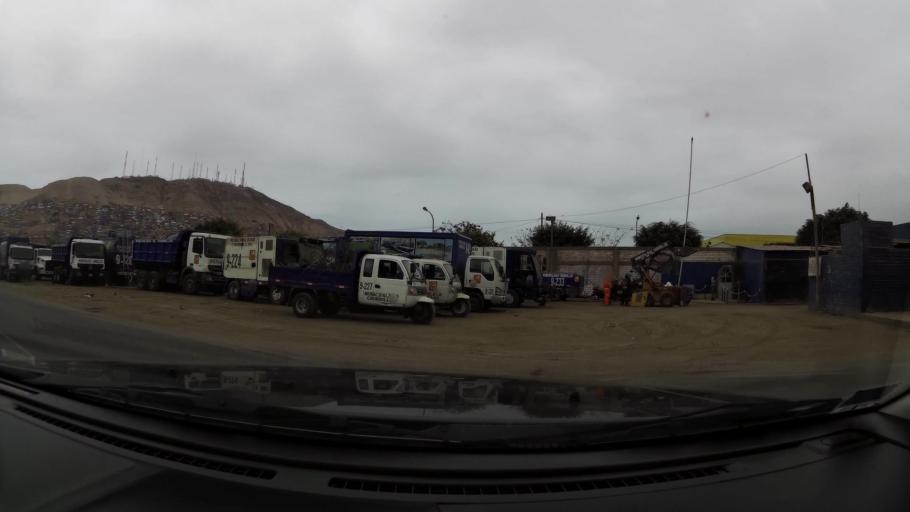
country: PE
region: Lima
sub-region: Lima
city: Surco
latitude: -12.1823
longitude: -77.0133
